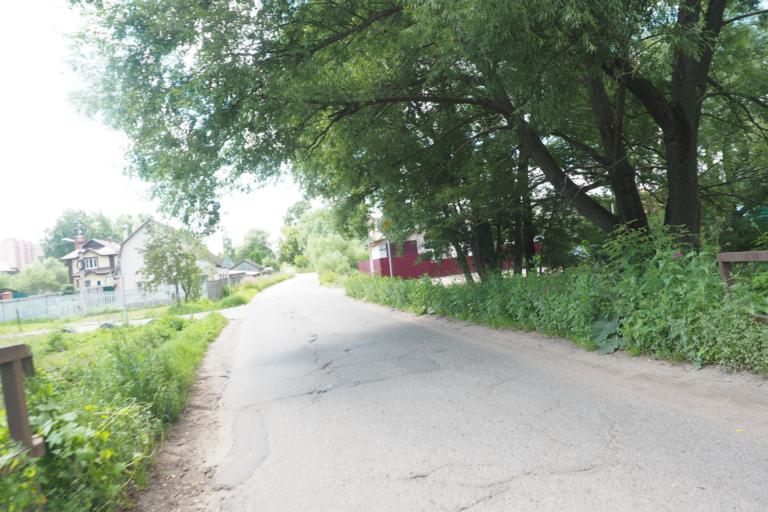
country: RU
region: Moskovskaya
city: Ramenskoye
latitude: 55.5828
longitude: 38.2561
